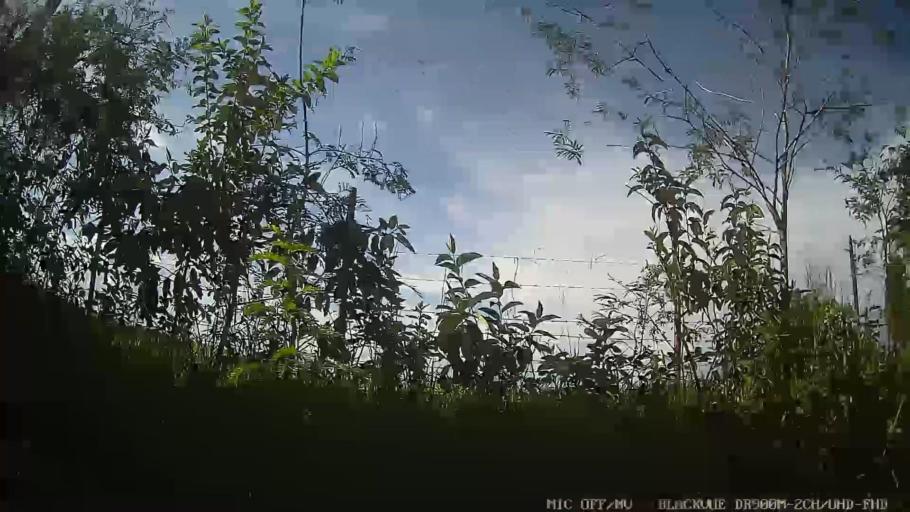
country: BR
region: Sao Paulo
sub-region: Tiete
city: Tiete
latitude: -23.0847
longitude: -47.6859
